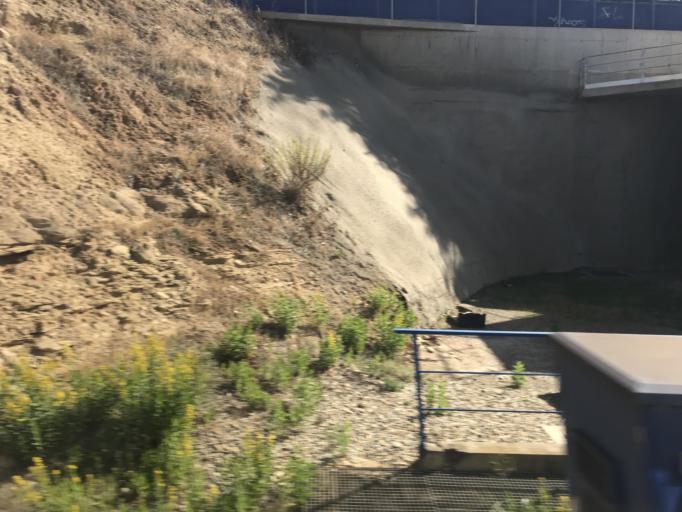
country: ES
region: Catalonia
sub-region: Provincia de Lleida
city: Lleida
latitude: 41.6217
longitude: 0.6096
